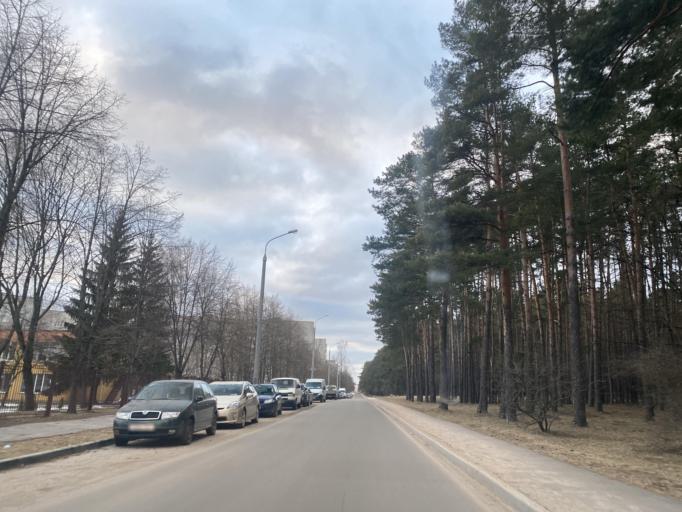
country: BY
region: Minsk
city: Borovlyany
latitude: 53.9536
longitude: 27.6387
